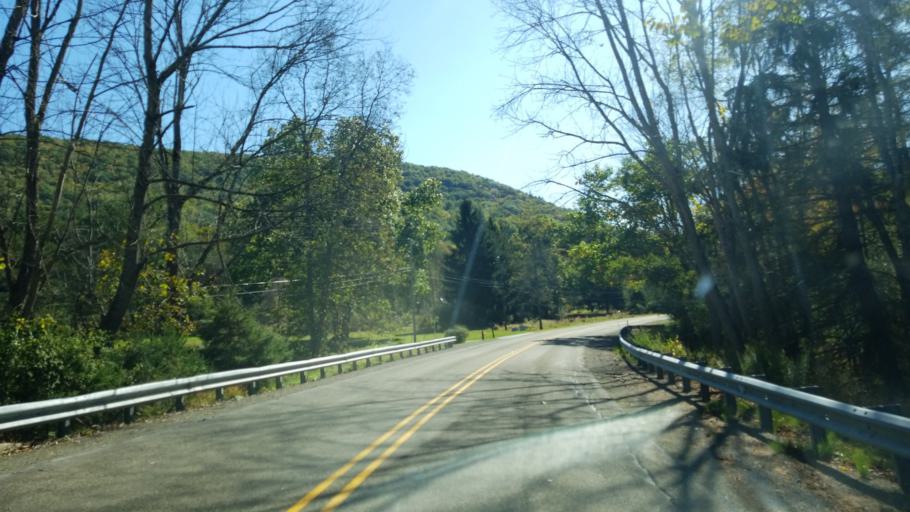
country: US
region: Pennsylvania
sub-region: Elk County
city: Saint Marys
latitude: 41.2842
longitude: -78.3938
